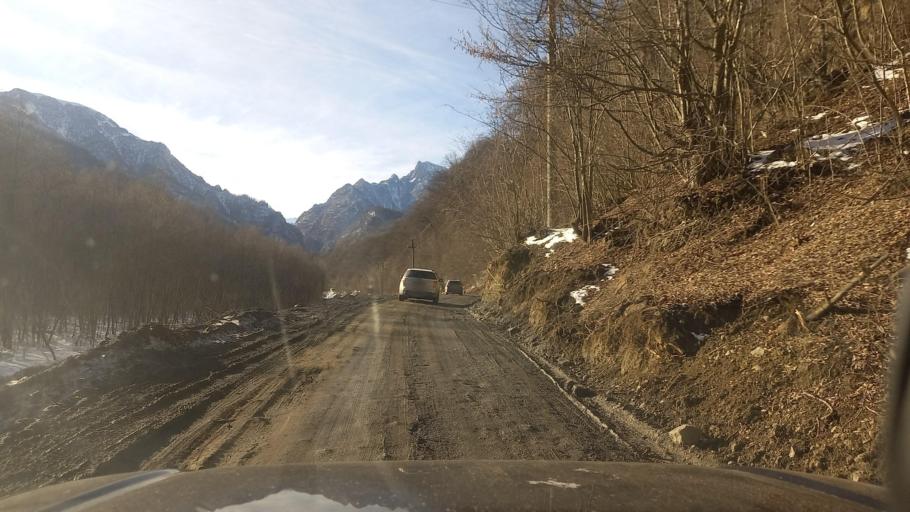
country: RU
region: North Ossetia
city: Gizel'
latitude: 42.9262
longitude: 44.5411
